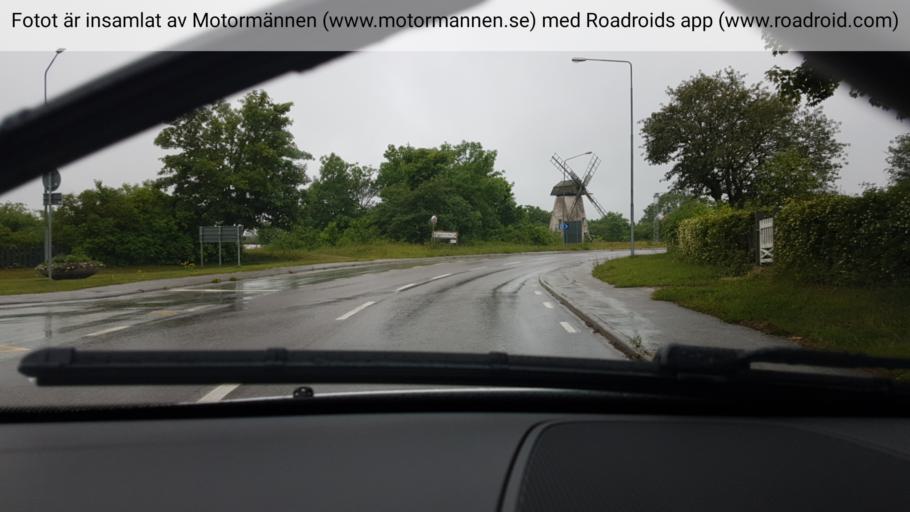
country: SE
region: Gotland
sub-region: Gotland
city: Slite
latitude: 57.8615
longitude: 19.0540
